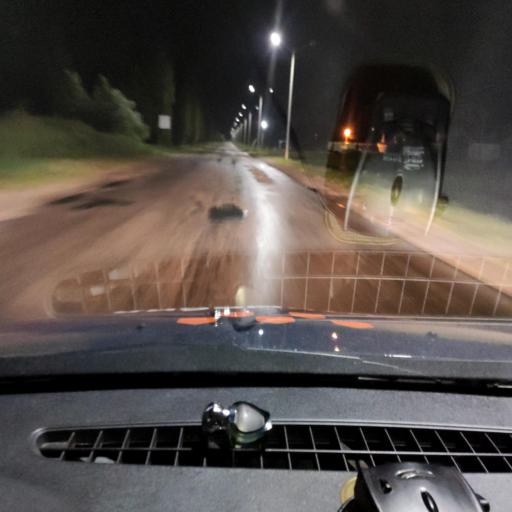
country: RU
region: Voronezj
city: Khrenovoye
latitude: 51.1189
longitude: 40.2643
